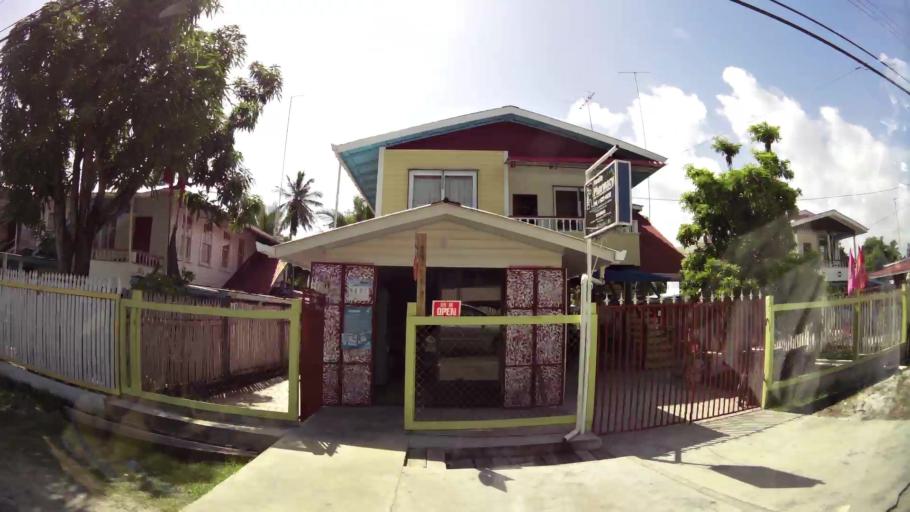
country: GY
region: Demerara-Mahaica
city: Mahaica Village
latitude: 6.7525
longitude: -57.9933
